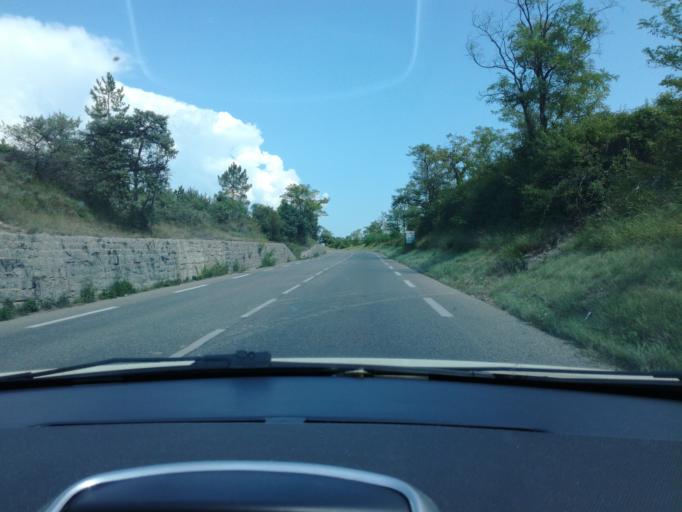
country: FR
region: Rhone-Alpes
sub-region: Departement de l'Ardeche
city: Ruoms
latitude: 44.4953
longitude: 4.3828
